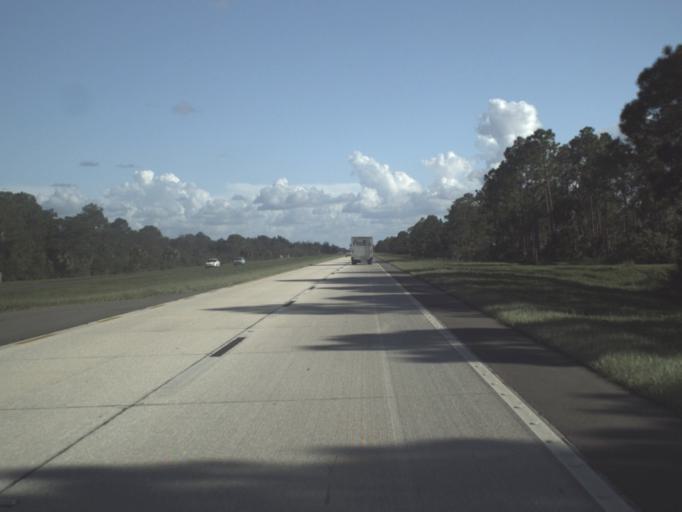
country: US
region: Florida
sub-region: Lee County
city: Burnt Store Marina
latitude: 26.8226
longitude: -81.9652
